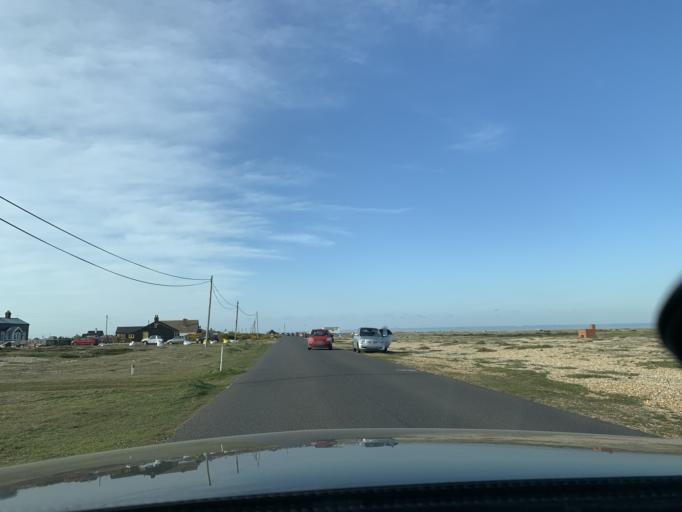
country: GB
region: England
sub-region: Kent
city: New Romney
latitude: 50.9214
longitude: 0.9766
